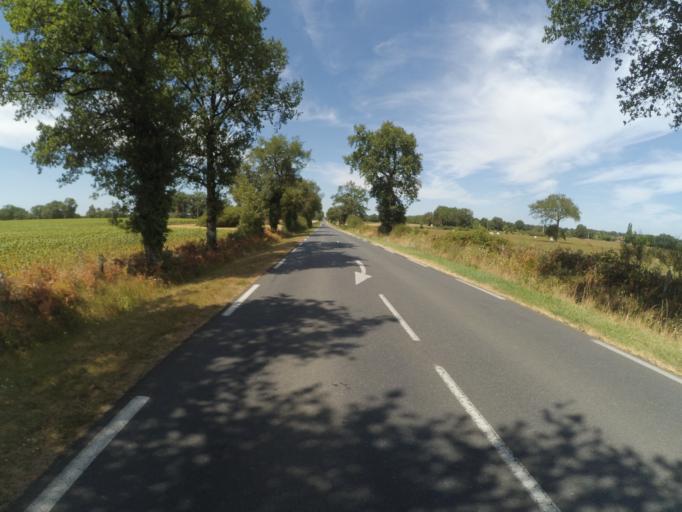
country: FR
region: Poitou-Charentes
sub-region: Departement de la Vienne
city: Availles-Limouzine
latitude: 46.0850
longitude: 0.5876
